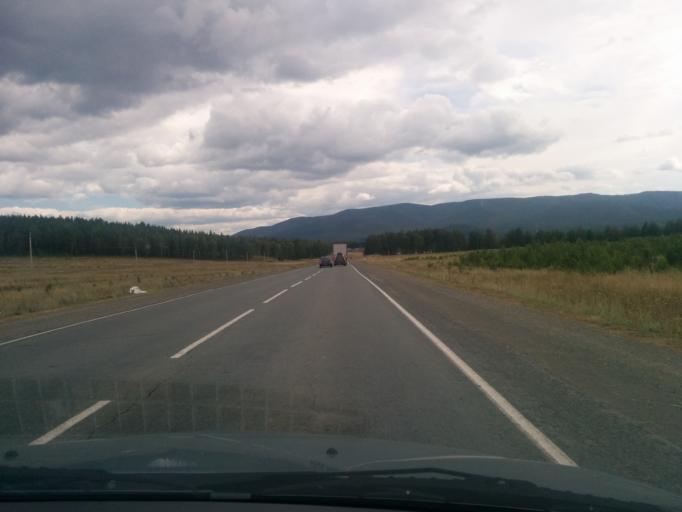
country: RU
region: Bashkortostan
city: Lomovka
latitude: 53.8921
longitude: 58.0942
